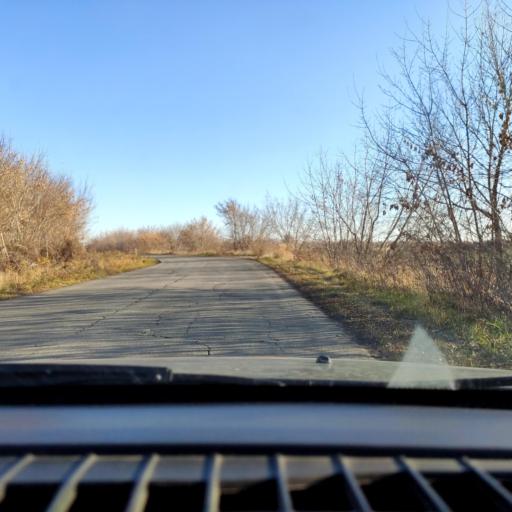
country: RU
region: Samara
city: Tol'yatti
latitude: 53.6329
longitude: 49.3043
